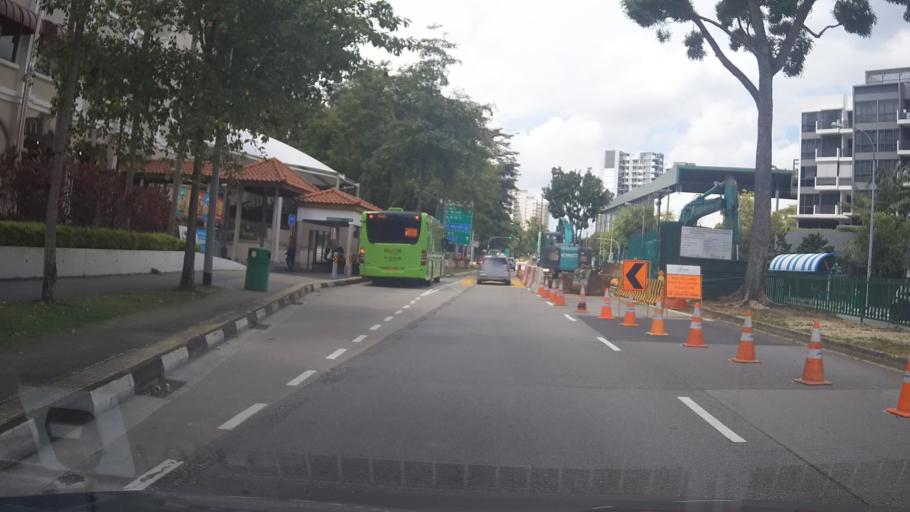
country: MY
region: Johor
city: Kampung Pasir Gudang Baru
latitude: 1.3786
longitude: 103.9430
